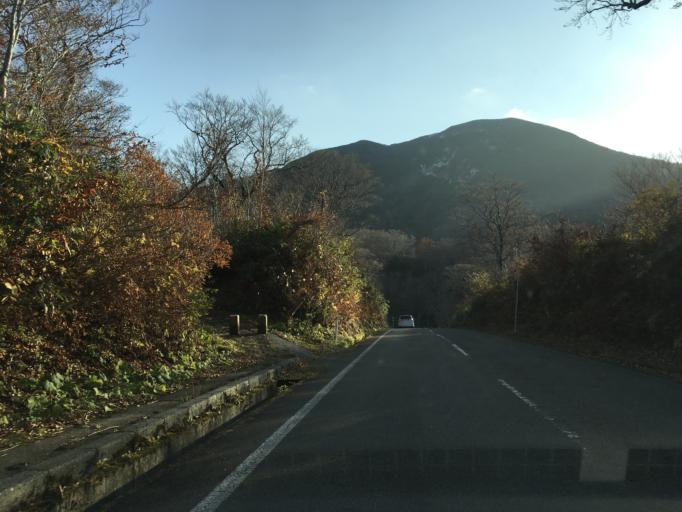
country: JP
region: Akita
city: Yuzawa
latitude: 38.9772
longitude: 140.7552
